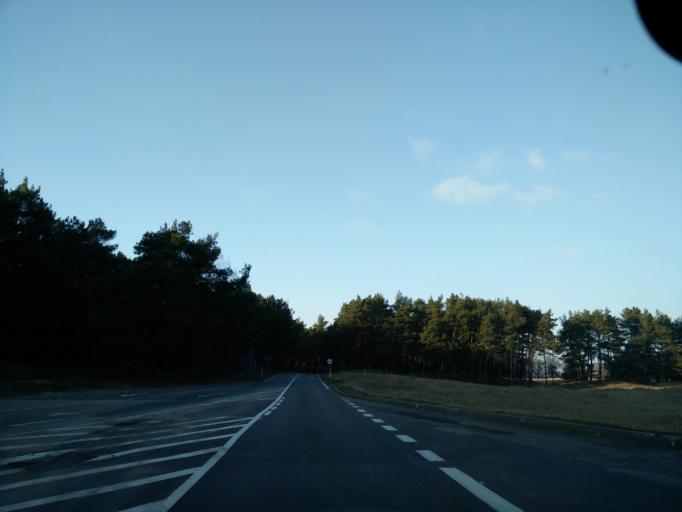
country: LT
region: Klaipedos apskritis
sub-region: Klaipeda
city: Klaipeda
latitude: 55.6335
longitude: 21.1303
